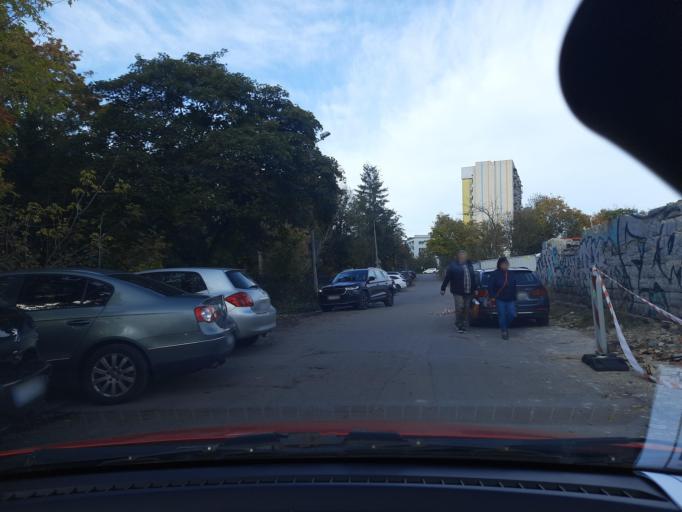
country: PL
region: Kujawsko-Pomorskie
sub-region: Torun
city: Torun
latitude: 53.0181
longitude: 18.5973
